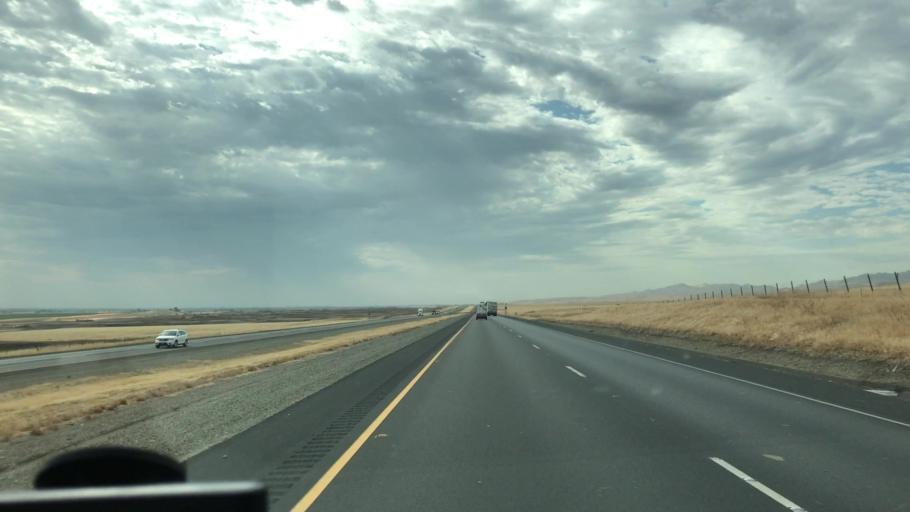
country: US
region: California
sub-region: San Joaquin County
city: Tracy
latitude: 37.6900
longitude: -121.4869
